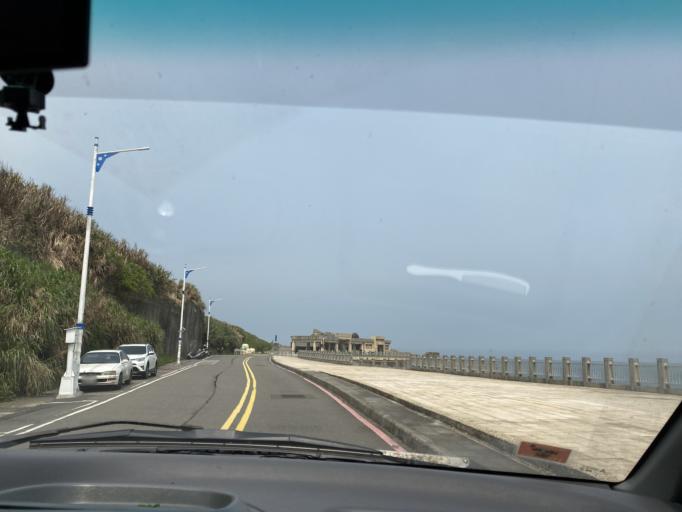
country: TW
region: Taiwan
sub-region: Keelung
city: Keelung
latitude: 25.1697
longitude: 121.7086
